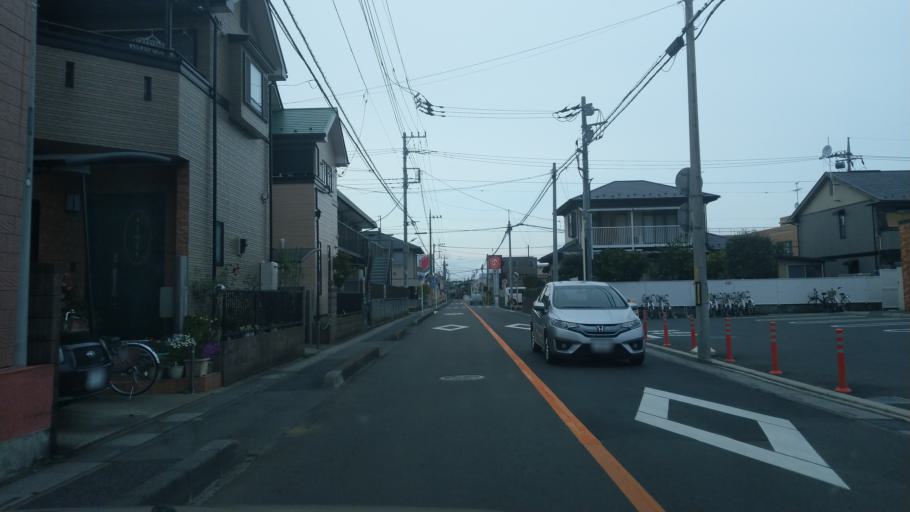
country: JP
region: Saitama
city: Ageoshimo
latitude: 35.9457
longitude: 139.6029
